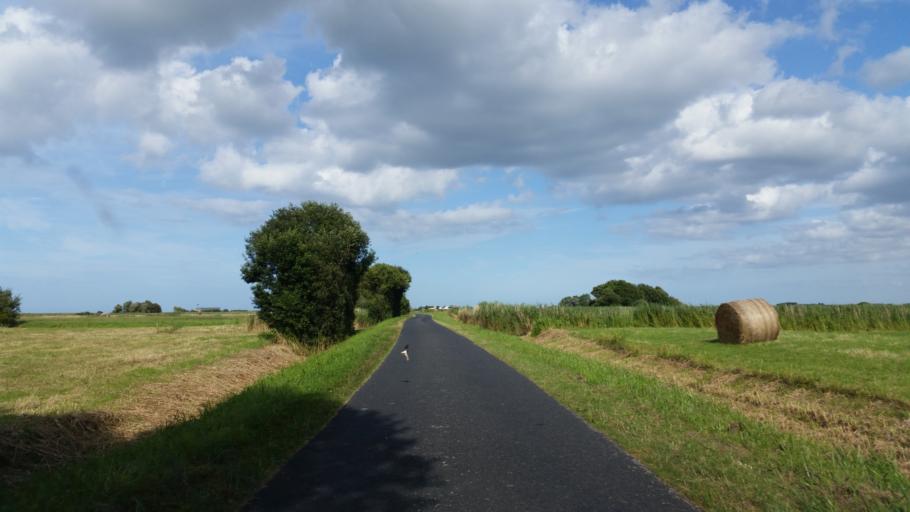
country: FR
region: Lower Normandy
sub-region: Departement de la Manche
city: Sainte-Mere-Eglise
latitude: 49.4522
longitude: -1.2463
